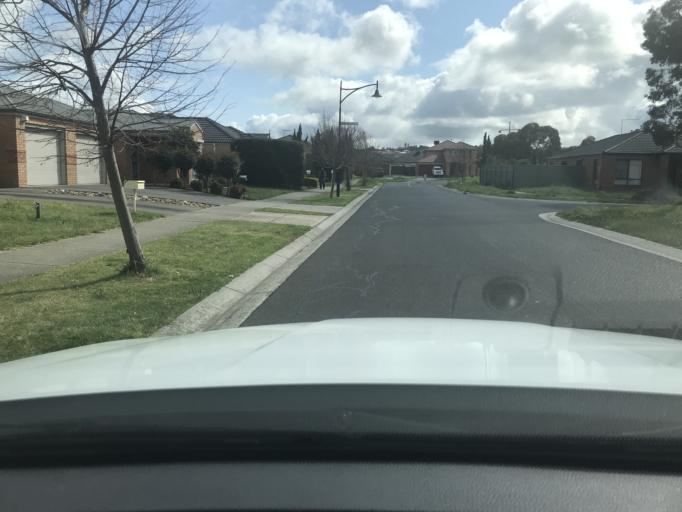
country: AU
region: Victoria
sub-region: Hume
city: Craigieburn
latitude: -37.5833
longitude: 144.9280
